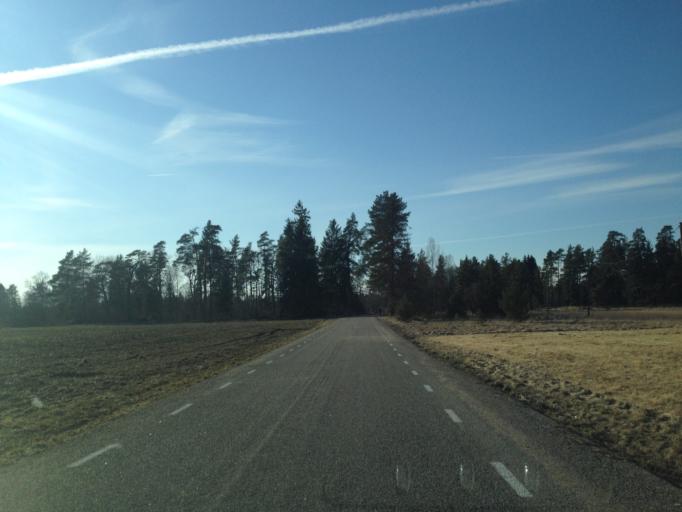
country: EE
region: Harju
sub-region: Nissi vald
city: Turba
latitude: 59.1423
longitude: 24.1613
